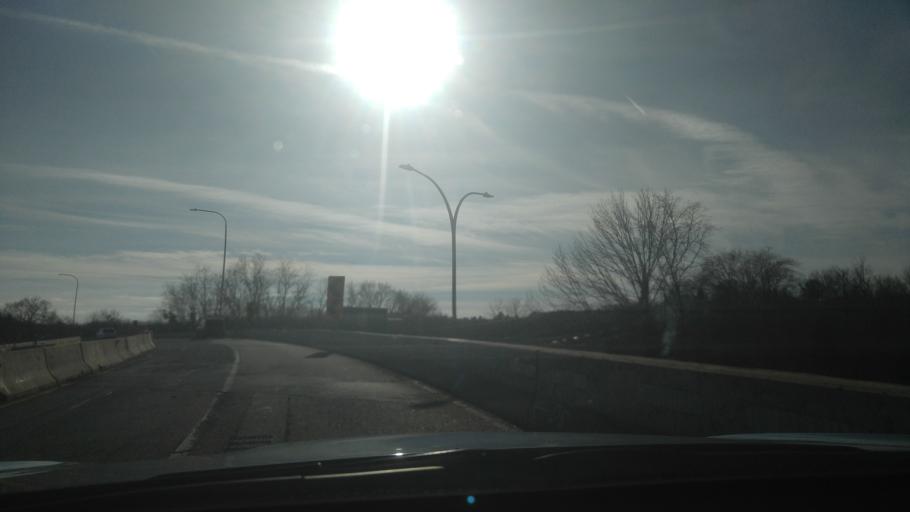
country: US
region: Rhode Island
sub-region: Providence County
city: Cumberland Hill
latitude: 41.9513
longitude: -71.4850
